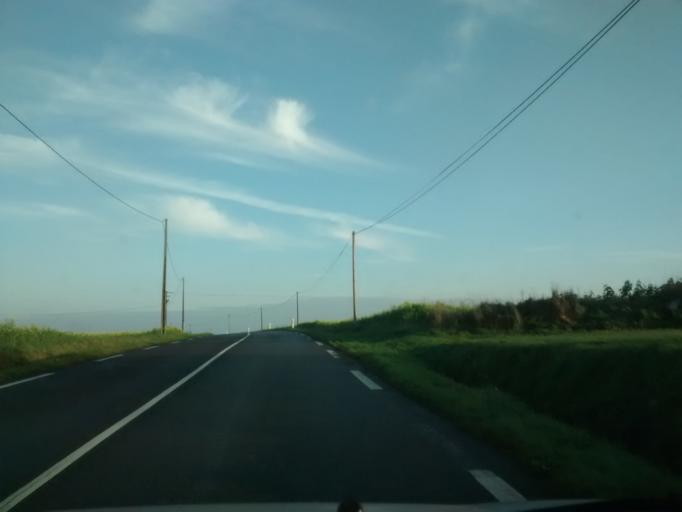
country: FR
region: Brittany
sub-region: Departement d'Ille-et-Vilaine
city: Antrain
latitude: 48.4673
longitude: -1.4768
